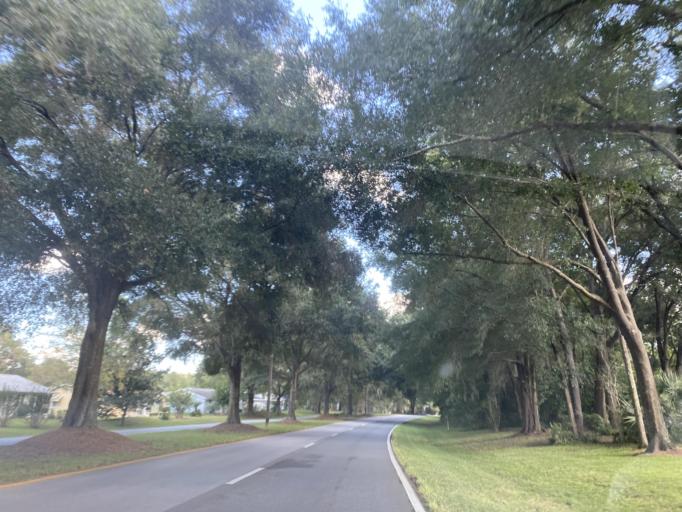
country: US
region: Florida
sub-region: Marion County
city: Ocala
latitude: 29.0569
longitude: -82.2558
